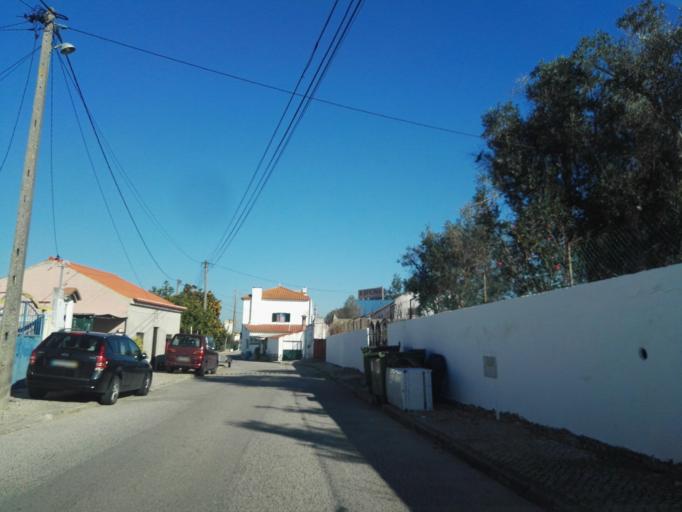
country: PT
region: Santarem
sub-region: Benavente
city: Samora Correia
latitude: 38.9252
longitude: -8.8900
